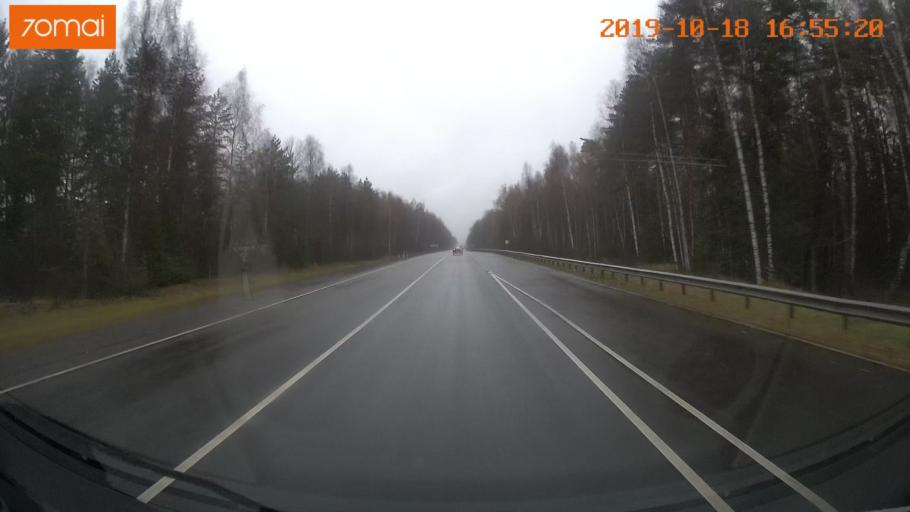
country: RU
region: Ivanovo
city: Novoye Leushino
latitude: 56.6424
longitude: 40.5784
